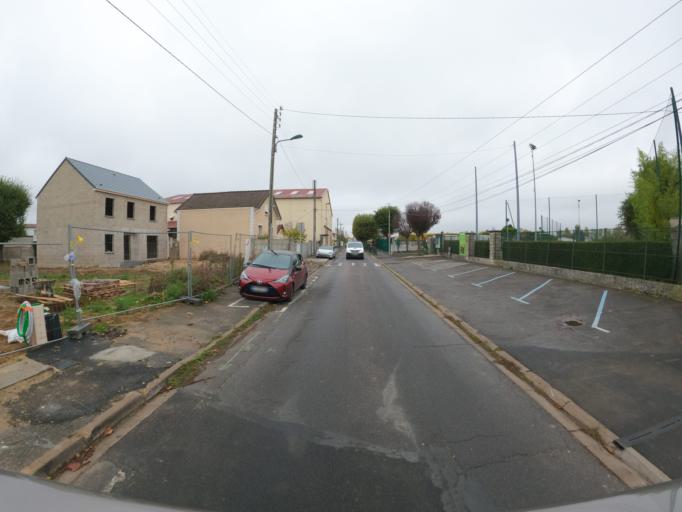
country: FR
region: Ile-de-France
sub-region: Departement du Val-de-Marne
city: Ormesson-sur-Marne
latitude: 48.7890
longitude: 2.5444
